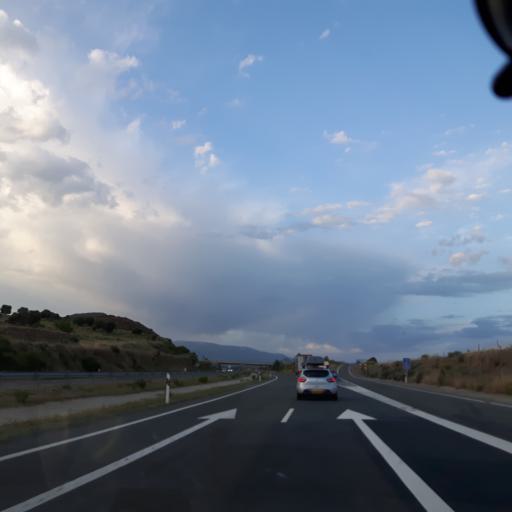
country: ES
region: Castille and Leon
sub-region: Provincia de Salamanca
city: Fuentes de Bejar
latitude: 40.5271
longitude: -5.6708
